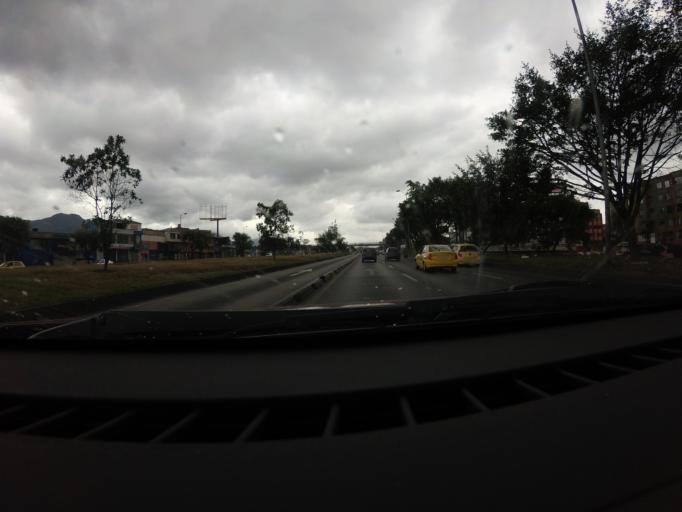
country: CO
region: Bogota D.C.
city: Bogota
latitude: 4.6612
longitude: -74.0769
